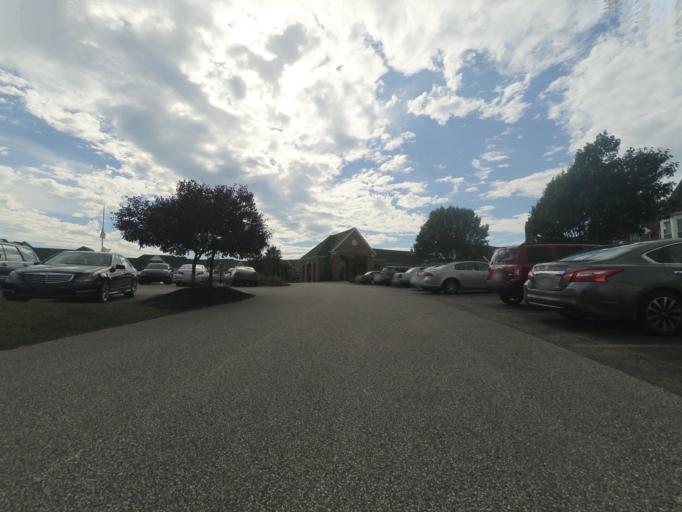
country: US
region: West Virginia
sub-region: Cabell County
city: Huntington
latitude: 38.3908
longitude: -82.4618
